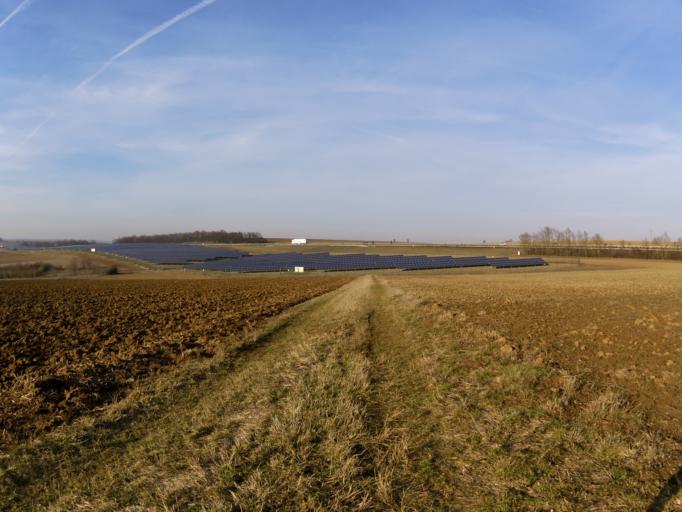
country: DE
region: Bavaria
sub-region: Regierungsbezirk Unterfranken
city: Kurnach
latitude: 49.8329
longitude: 10.0337
